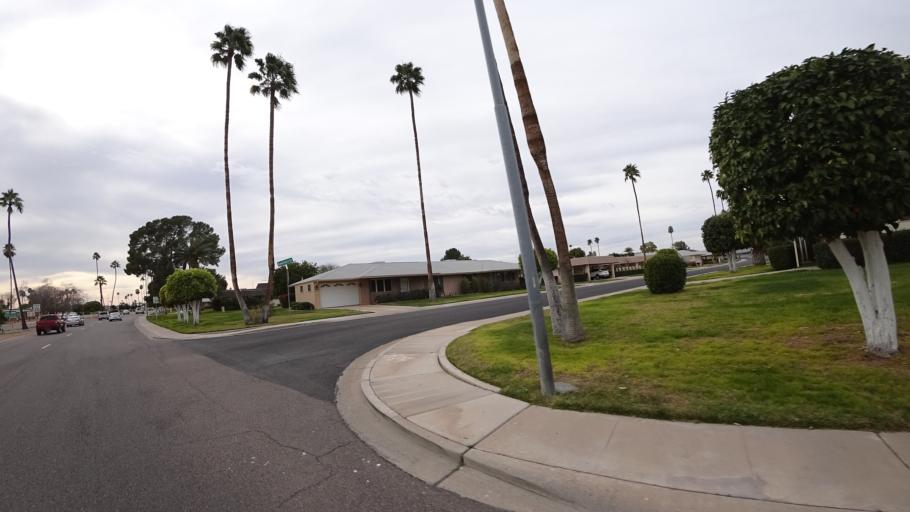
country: US
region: Arizona
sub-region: Maricopa County
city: Sun City
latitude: 33.6068
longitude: -112.2744
